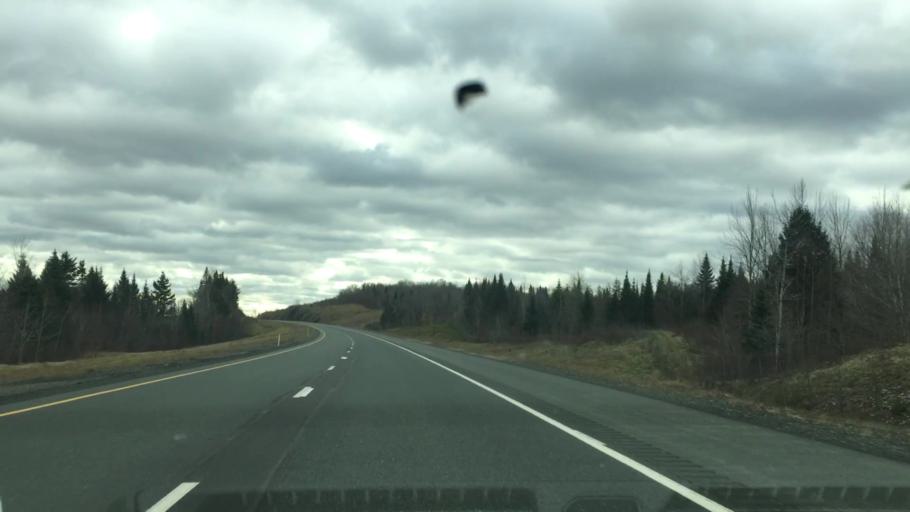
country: US
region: Maine
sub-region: Aroostook County
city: Fort Fairfield
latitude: 46.6399
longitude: -67.7444
